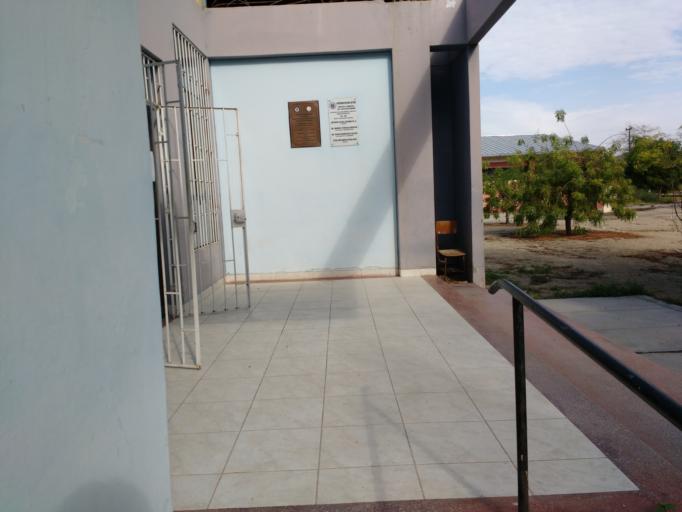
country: PE
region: Piura
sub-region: Provincia de Piura
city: Piura
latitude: -5.1807
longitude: -80.6220
